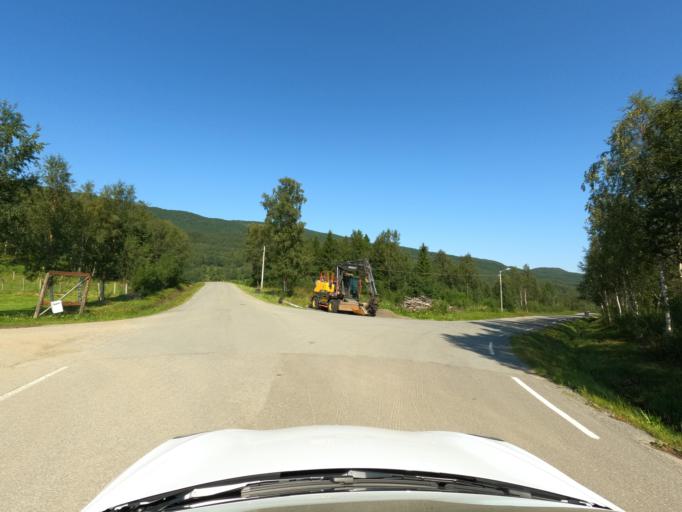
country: NO
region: Nordland
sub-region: Ballangen
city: Ballangen
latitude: 68.3466
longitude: 16.8047
